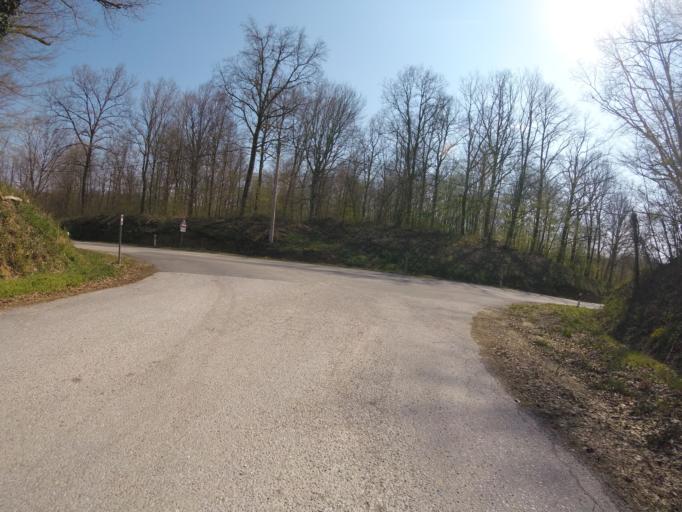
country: HR
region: Grad Zagreb
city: Strmec
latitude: 45.5397
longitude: 15.9035
